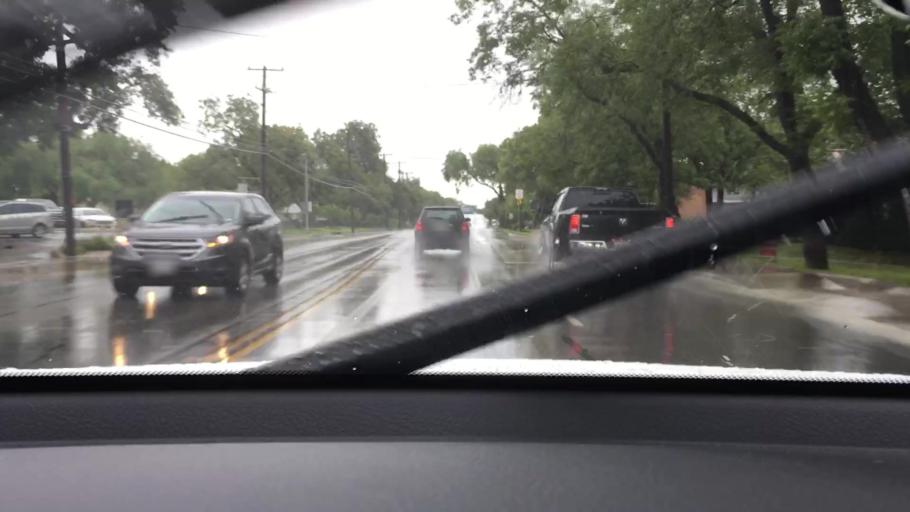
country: US
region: Texas
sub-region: Bexar County
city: Alamo Heights
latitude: 29.4898
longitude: -98.4666
